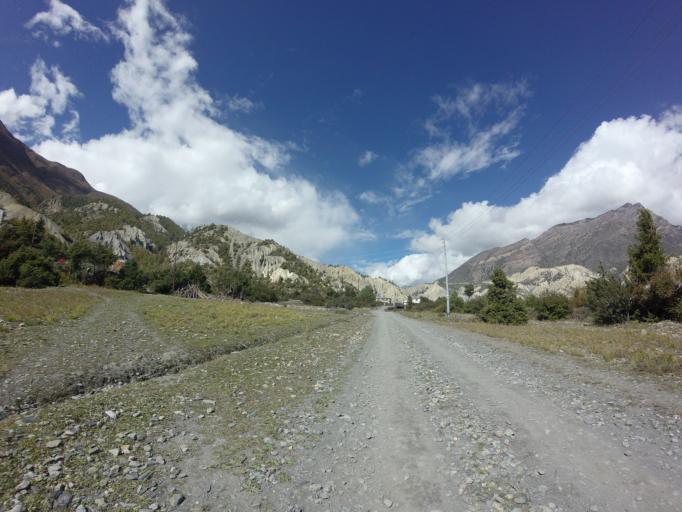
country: NP
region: Western Region
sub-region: Gandaki Zone
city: Nawal
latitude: 28.6368
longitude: 84.0933
